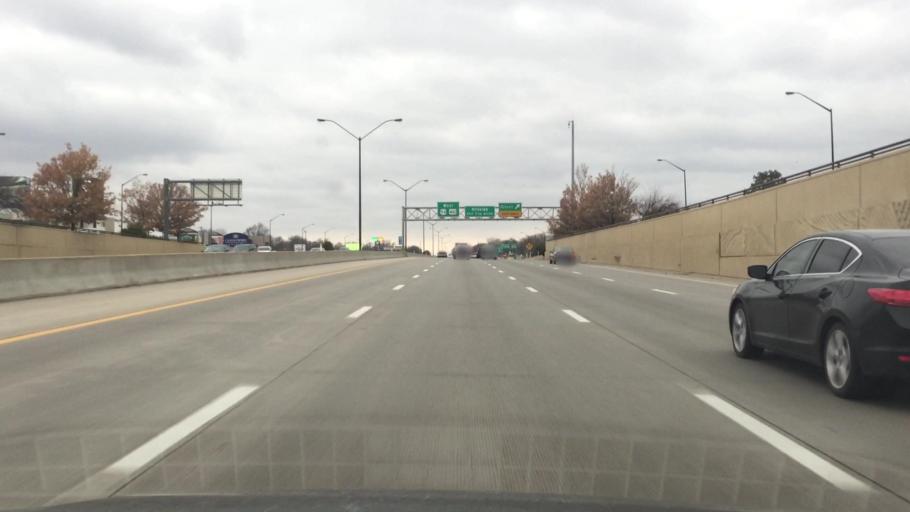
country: US
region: Kansas
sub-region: Sedgwick County
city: Wichita
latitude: 37.6796
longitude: -97.2726
